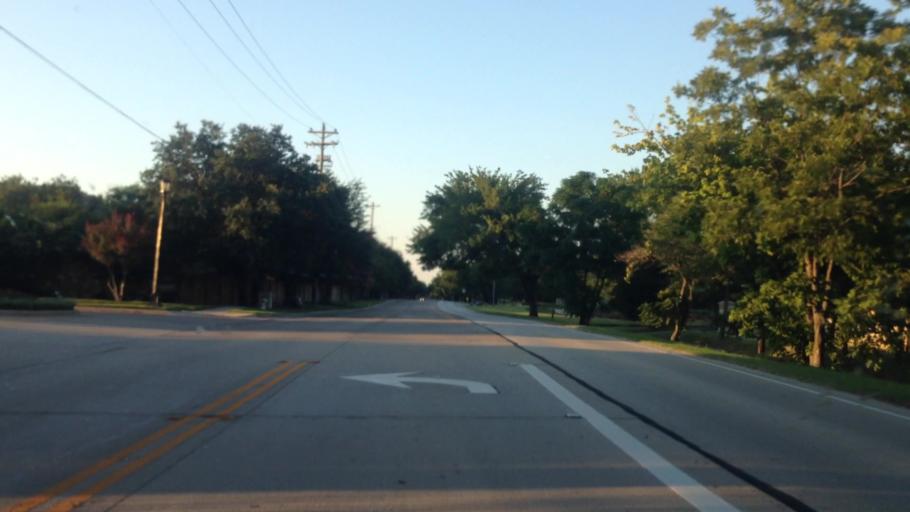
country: US
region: Texas
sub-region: Tarrant County
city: Southlake
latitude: 32.9368
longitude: -97.1336
